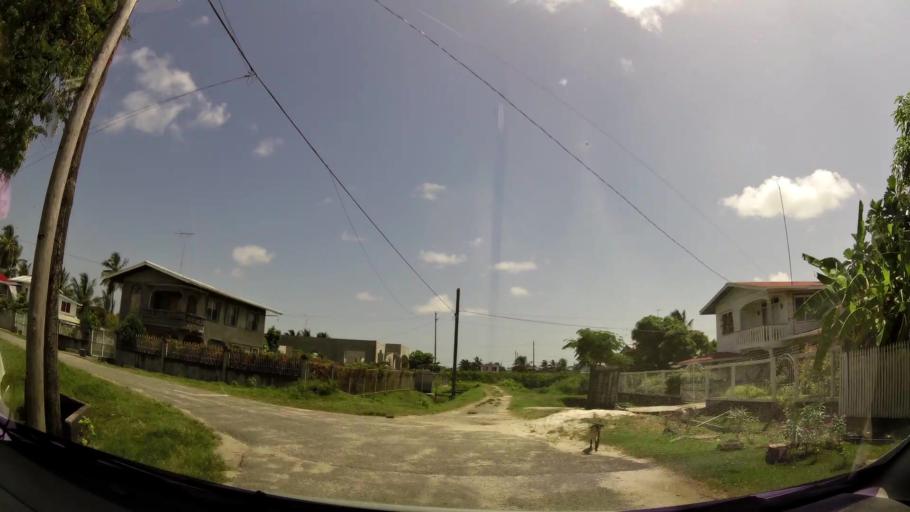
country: GY
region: Demerara-Mahaica
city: Mahaica Village
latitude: 6.7676
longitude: -58.0078
